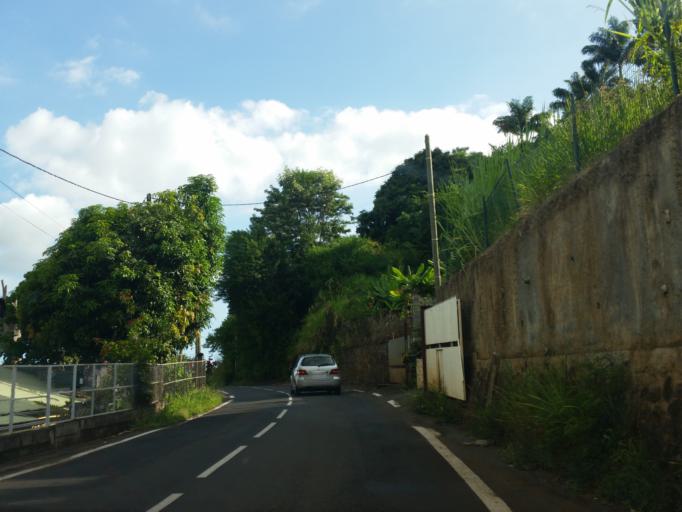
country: RE
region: Reunion
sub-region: Reunion
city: L'Entre-Deux
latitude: -21.2473
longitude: 55.4766
